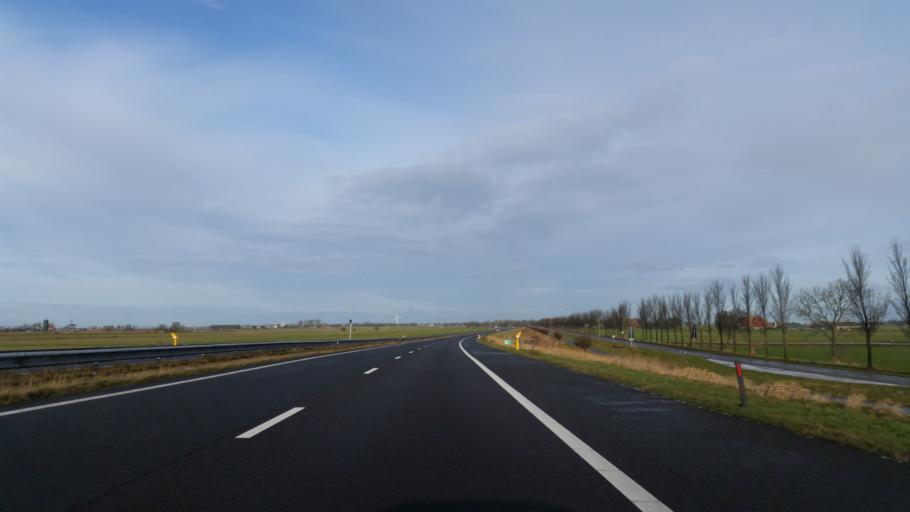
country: NL
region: Friesland
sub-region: Gemeente Boarnsterhim
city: Nes
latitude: 53.0068
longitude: 5.8720
